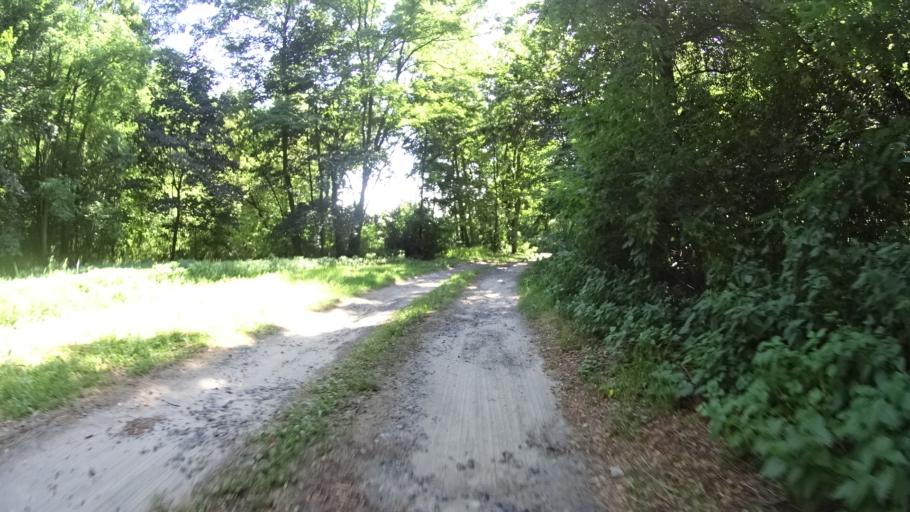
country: PL
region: Masovian Voivodeship
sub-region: Powiat bialobrzeski
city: Bialobrzegi
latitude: 51.6698
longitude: 20.9299
